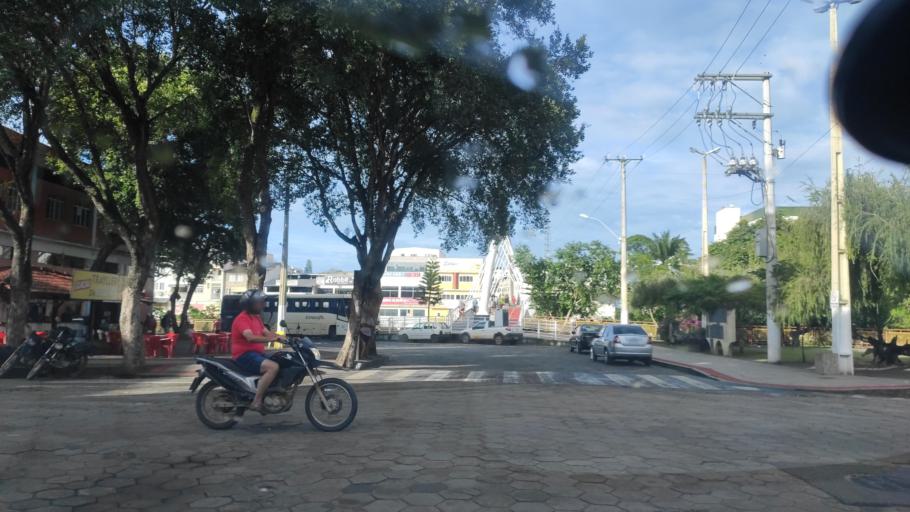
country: BR
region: Espirito Santo
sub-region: Nova Venecia
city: Nova Venecia
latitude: -18.7077
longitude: -40.4014
